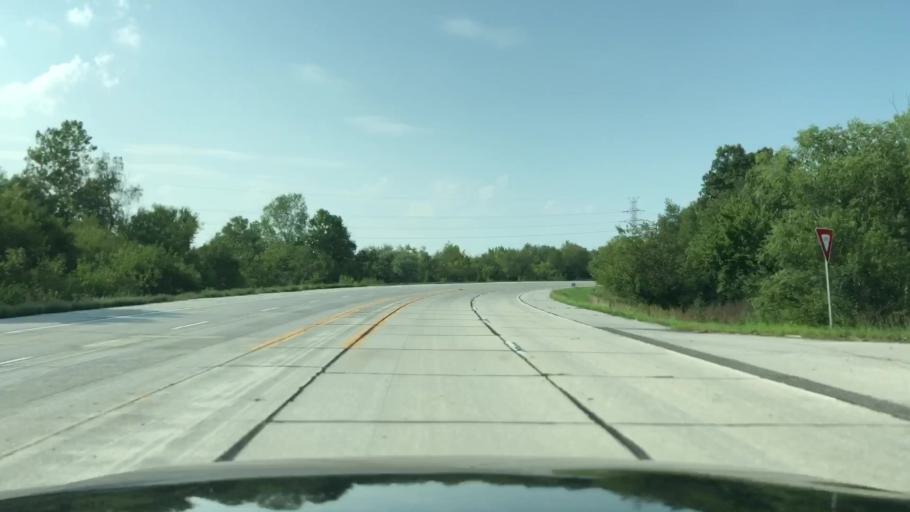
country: US
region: Missouri
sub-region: Saint Charles County
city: Lake Saint Louis
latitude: 38.8127
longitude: -90.8107
